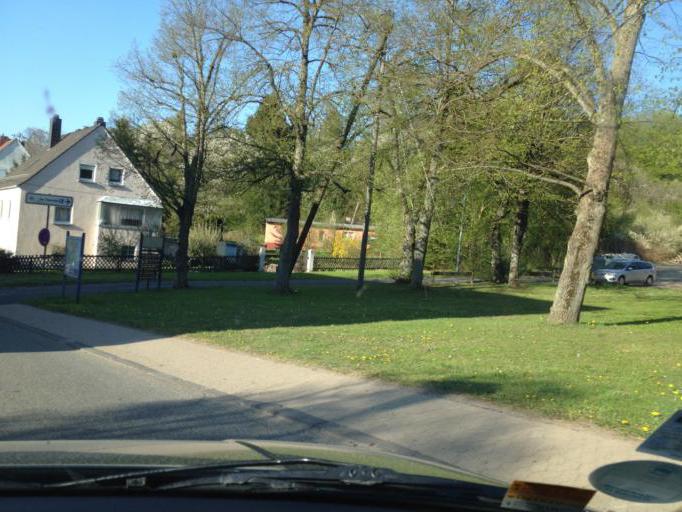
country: DE
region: Saarland
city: Sankt Wendel
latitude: 49.4698
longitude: 7.1759
